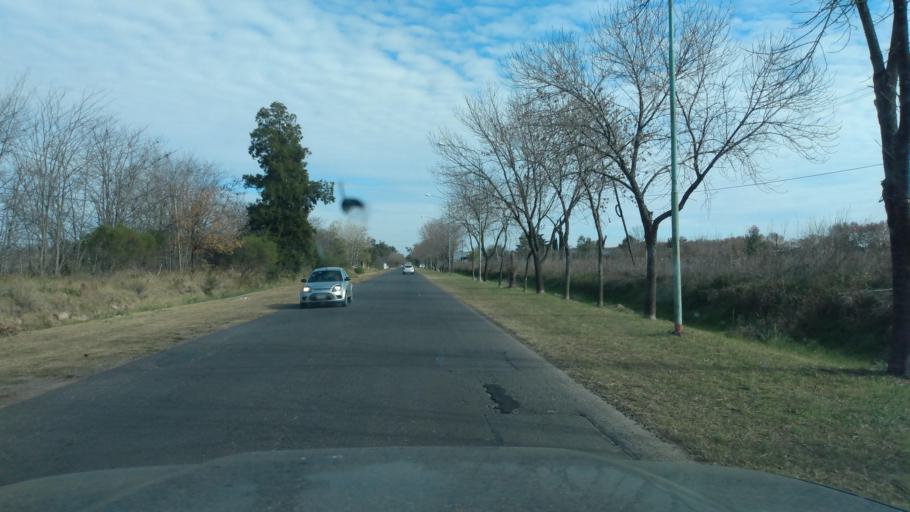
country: AR
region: Buenos Aires
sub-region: Partido de Lujan
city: Lujan
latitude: -34.5774
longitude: -59.1669
